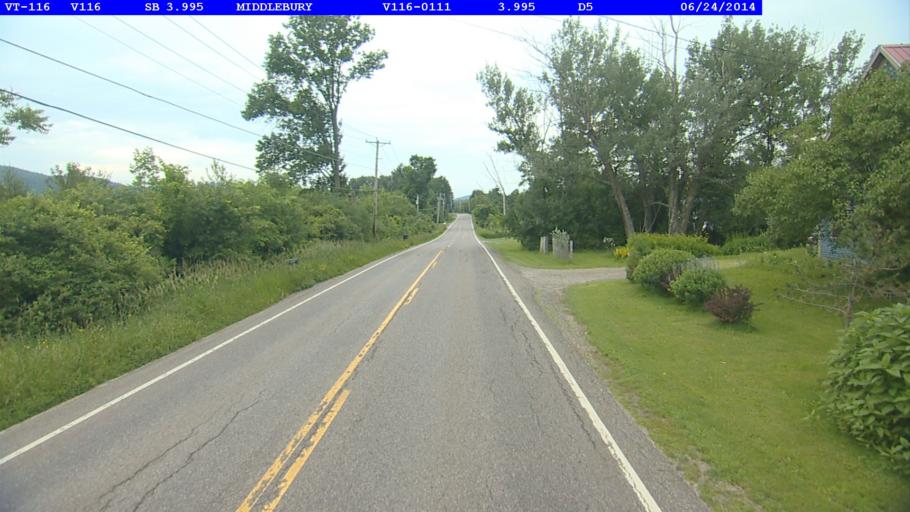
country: US
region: Vermont
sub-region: Addison County
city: Middlebury (village)
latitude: 44.0199
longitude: -73.1025
